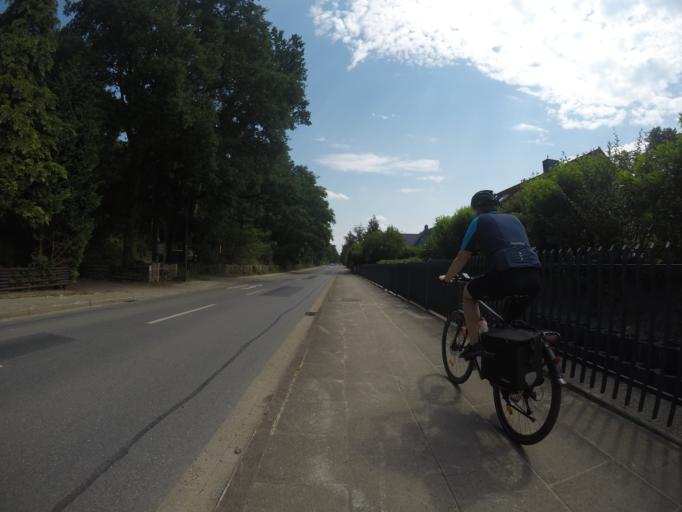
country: DE
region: Lower Saxony
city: Buchholz in der Nordheide
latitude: 53.2867
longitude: 9.8553
